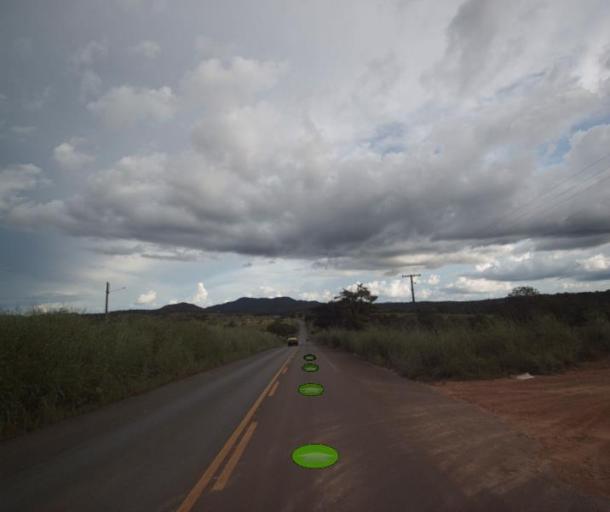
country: BR
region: Goias
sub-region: Niquelandia
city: Niquelandia
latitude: -14.4761
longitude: -48.4888
